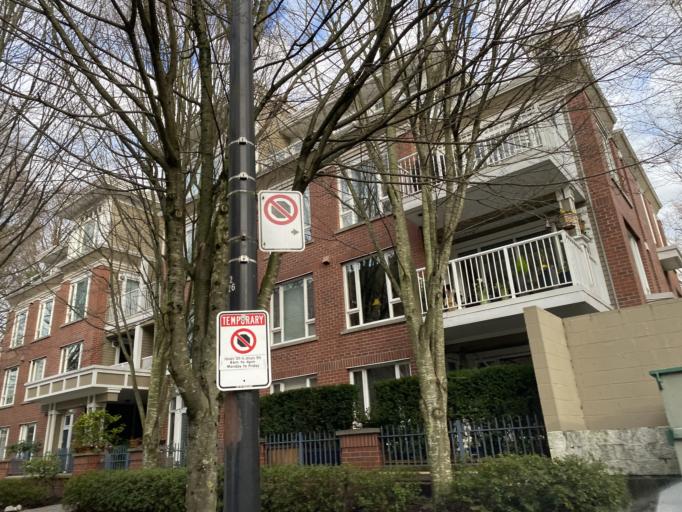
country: CA
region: British Columbia
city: West End
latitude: 49.2624
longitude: -123.1553
